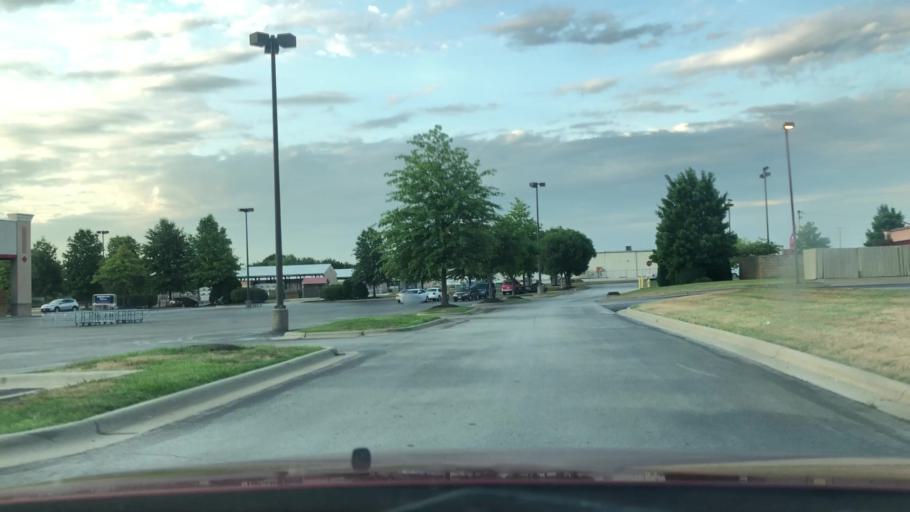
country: US
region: Missouri
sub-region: Greene County
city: Republic
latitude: 37.1310
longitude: -93.4602
